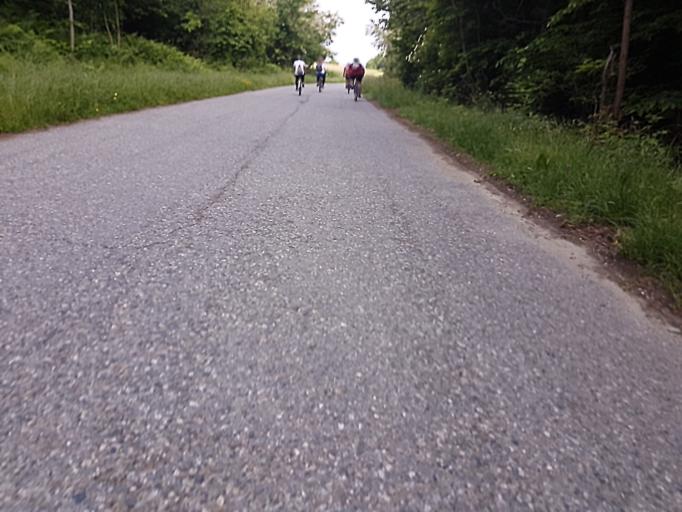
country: IT
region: Piedmont
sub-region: Provincia di Torino
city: Vialfre
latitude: 45.3804
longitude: 7.8246
